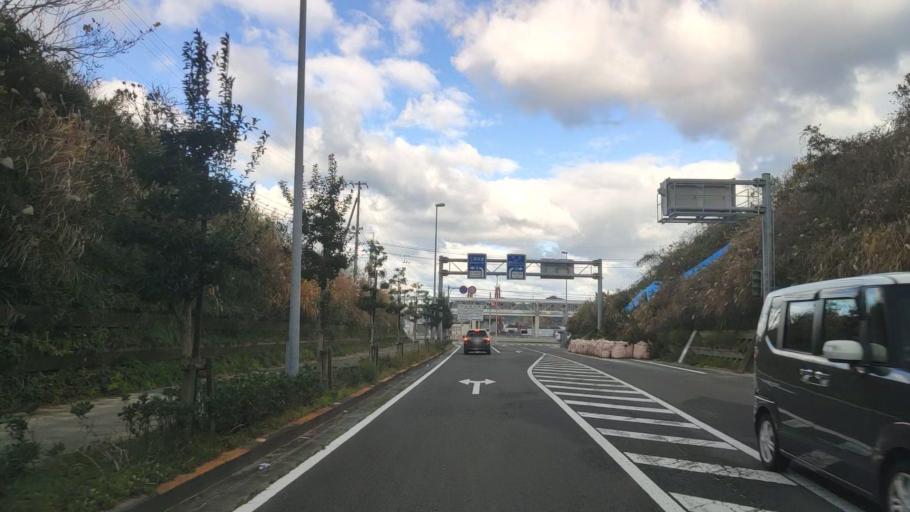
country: JP
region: Ehime
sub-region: Shikoku-chuo Shi
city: Matsuyama
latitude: 33.8882
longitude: 132.7063
